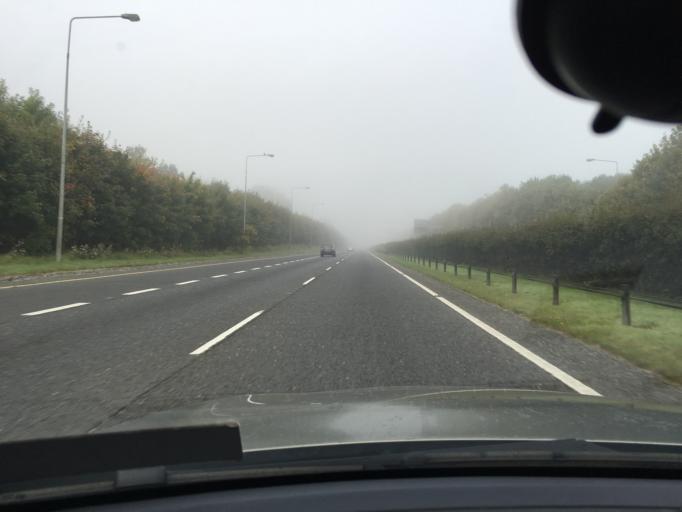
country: IE
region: Leinster
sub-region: Kildare
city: Maynooth
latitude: 53.3682
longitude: -6.5973
